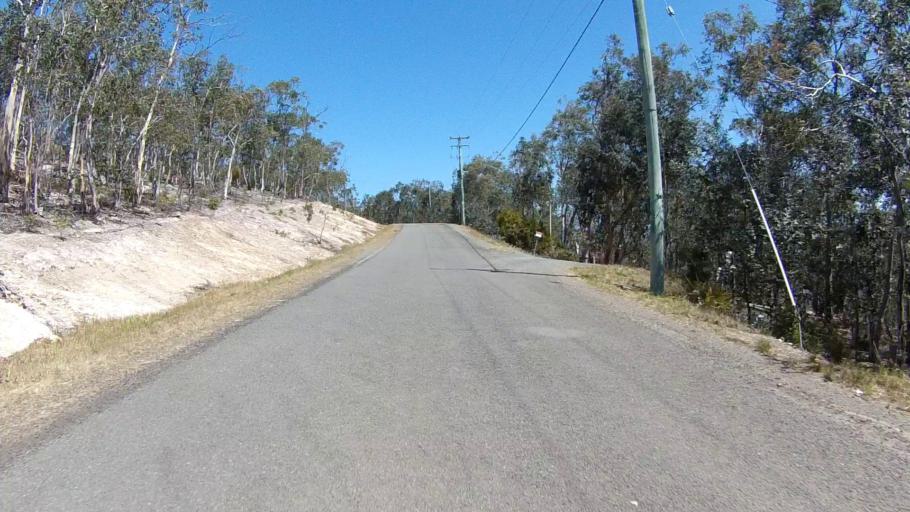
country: AU
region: Tasmania
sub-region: Clarence
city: Sandford
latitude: -42.9593
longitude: 147.4827
